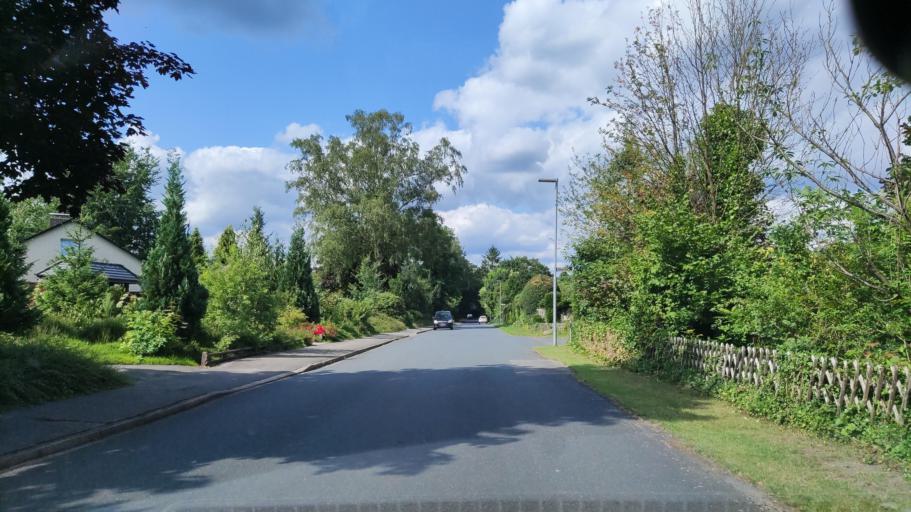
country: DE
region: Lower Saxony
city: Soltau
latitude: 53.0167
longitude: 9.8730
